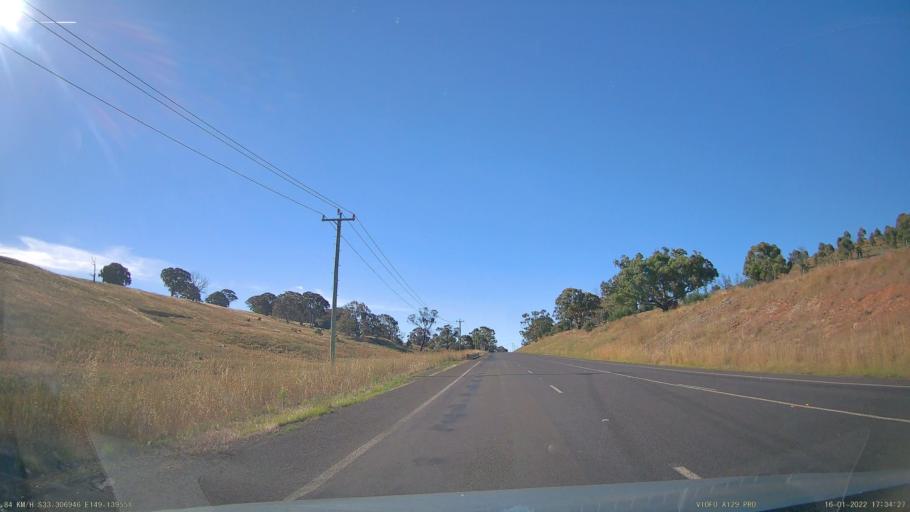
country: AU
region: New South Wales
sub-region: Orange Municipality
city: Orange
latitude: -33.3068
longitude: 149.1395
